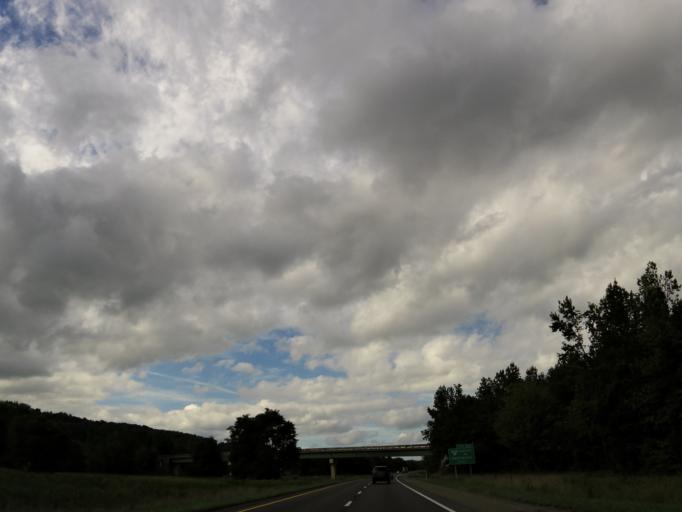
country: US
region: Tennessee
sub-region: Monroe County
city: Sweetwater
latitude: 35.6381
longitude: -84.4746
